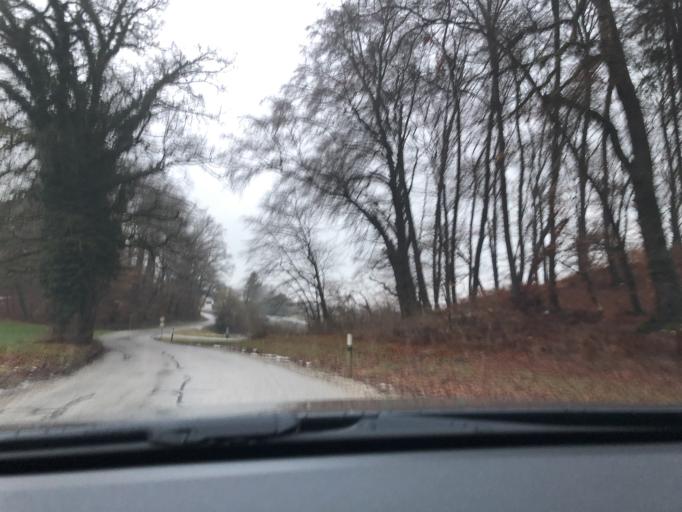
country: DE
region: Bavaria
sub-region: Upper Bavaria
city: Worthsee
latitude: 48.0784
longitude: 11.1834
